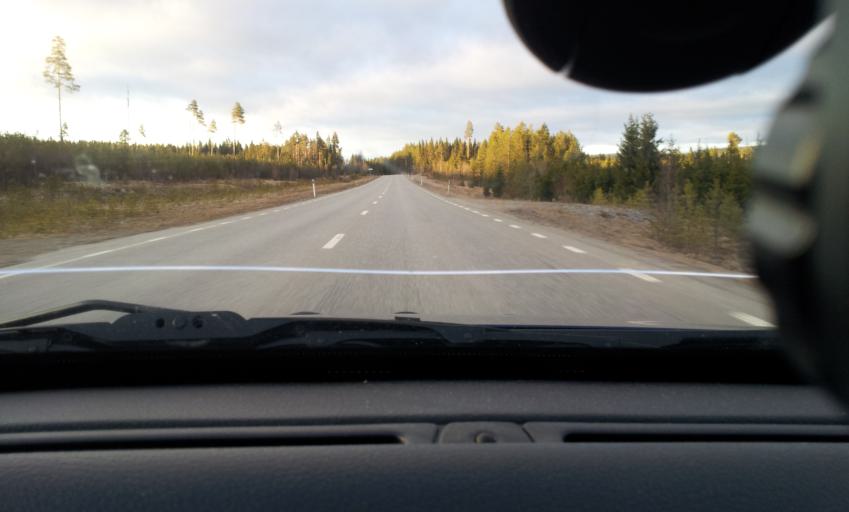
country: SE
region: Jaemtland
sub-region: Bergs Kommun
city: Hoverberg
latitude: 62.7119
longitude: 14.4128
